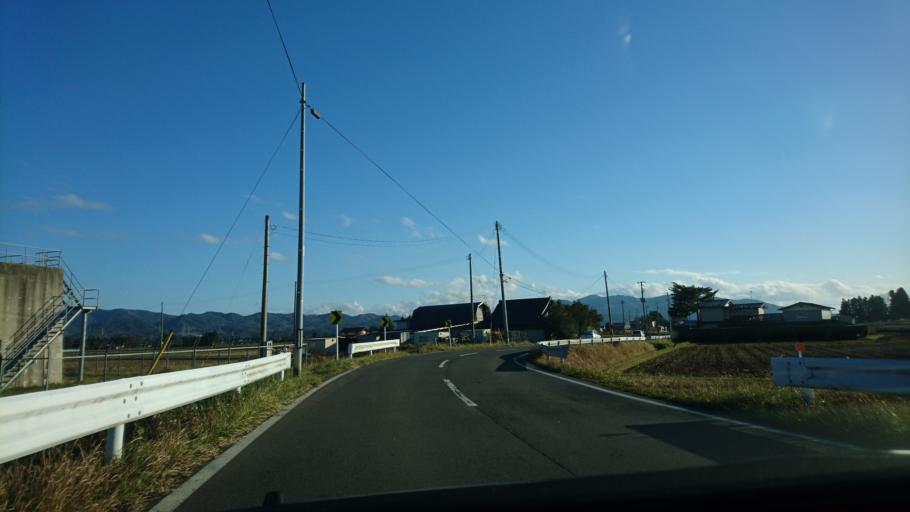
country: JP
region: Iwate
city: Mizusawa
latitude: 39.0995
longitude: 141.1585
